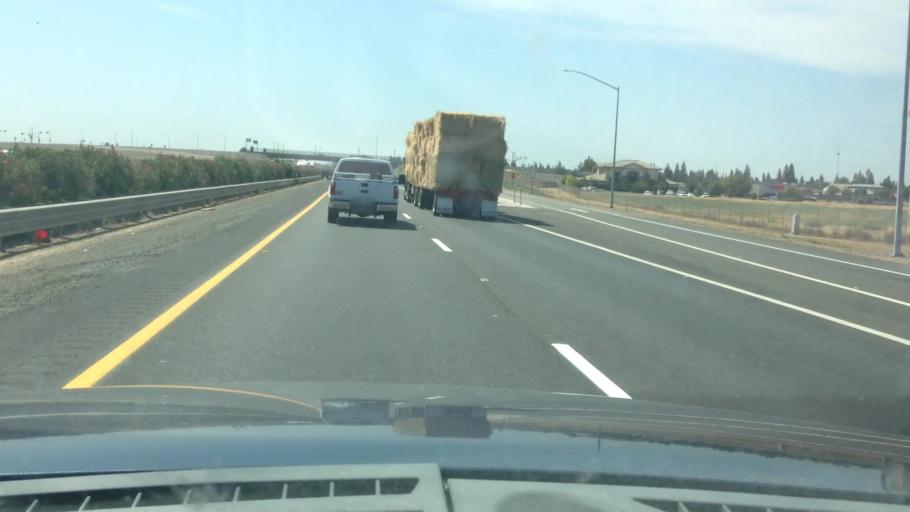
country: US
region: California
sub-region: Tulare County
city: Tulare
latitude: 36.2424
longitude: -119.3452
